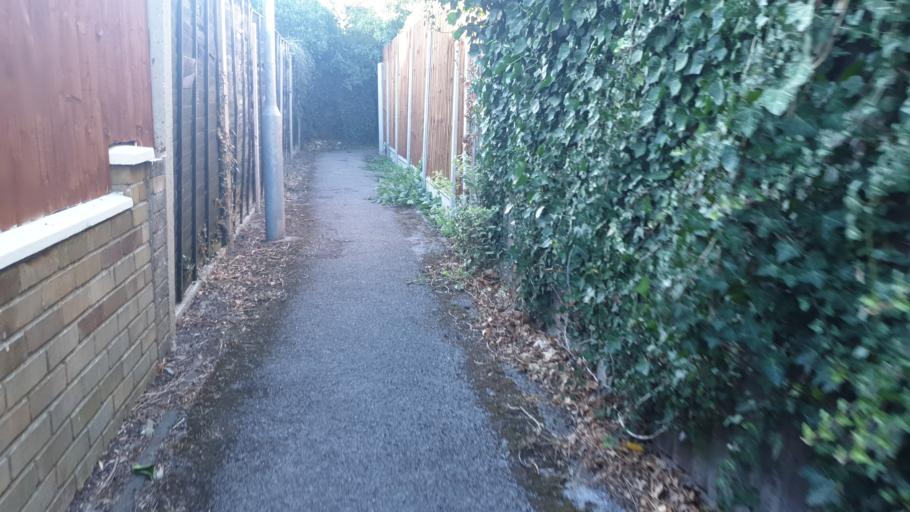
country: GB
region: England
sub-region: Essex
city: Clacton-on-Sea
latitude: 51.8061
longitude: 1.1785
